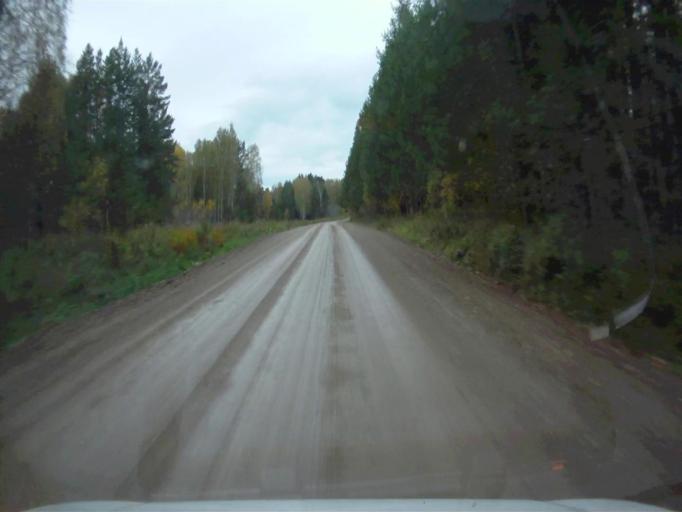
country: RU
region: Chelyabinsk
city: Nyazepetrovsk
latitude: 56.0955
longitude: 59.4014
